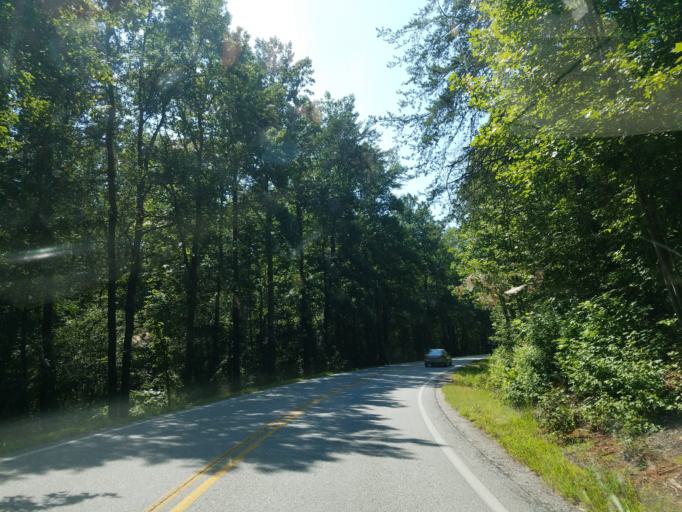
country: US
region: Georgia
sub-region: Lumpkin County
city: Dahlonega
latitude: 34.6253
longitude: -83.9423
